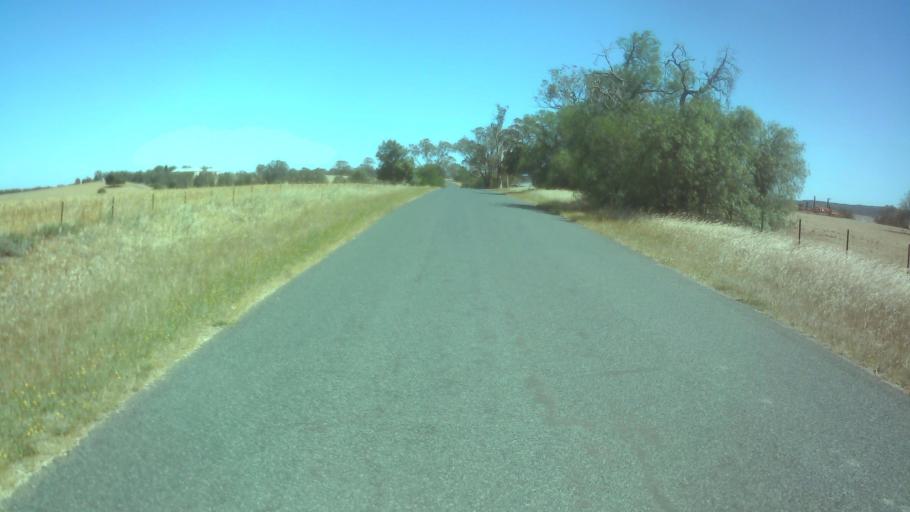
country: AU
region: New South Wales
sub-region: Weddin
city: Grenfell
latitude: -33.9509
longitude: 148.3968
